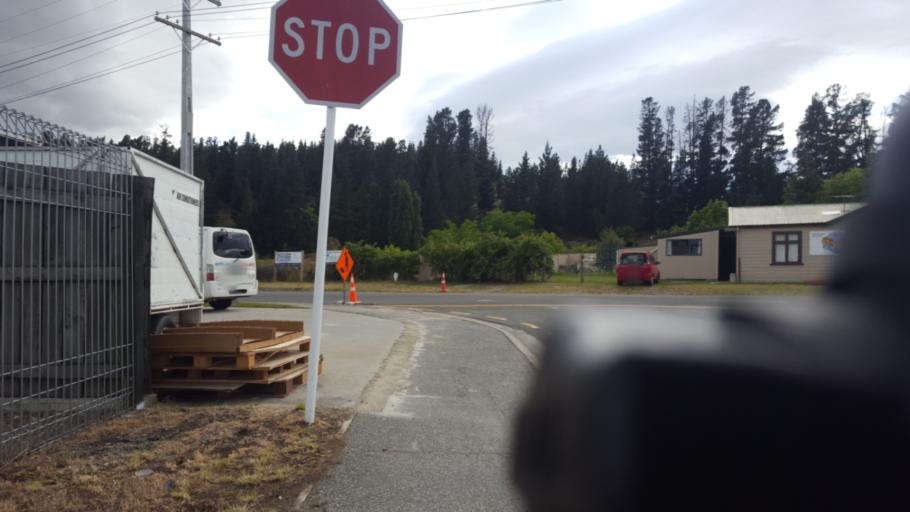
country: NZ
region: Otago
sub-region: Queenstown-Lakes District
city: Wanaka
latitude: -45.2452
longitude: 169.3963
